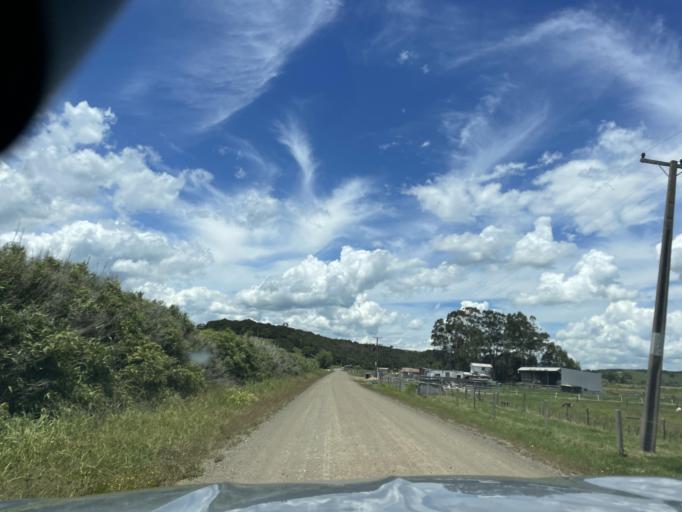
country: NZ
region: Northland
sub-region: Kaipara District
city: Dargaville
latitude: -35.8938
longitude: 173.9062
